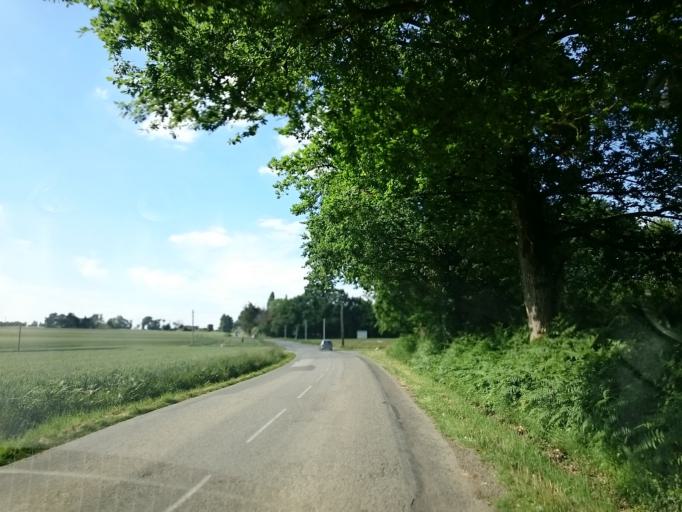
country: FR
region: Brittany
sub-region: Departement d'Ille-et-Vilaine
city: Chanteloup
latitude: 47.9777
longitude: -1.6118
